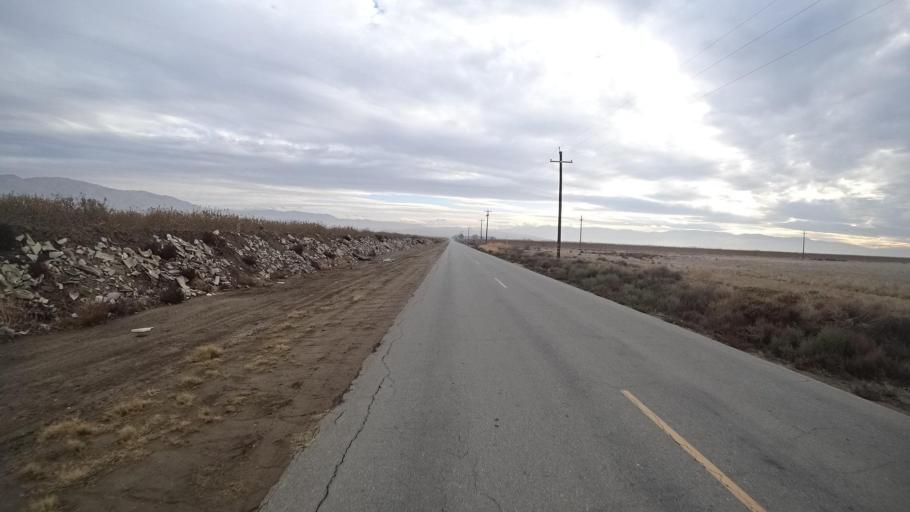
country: US
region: California
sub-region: Kern County
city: Arvin
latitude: 35.1740
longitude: -118.8239
